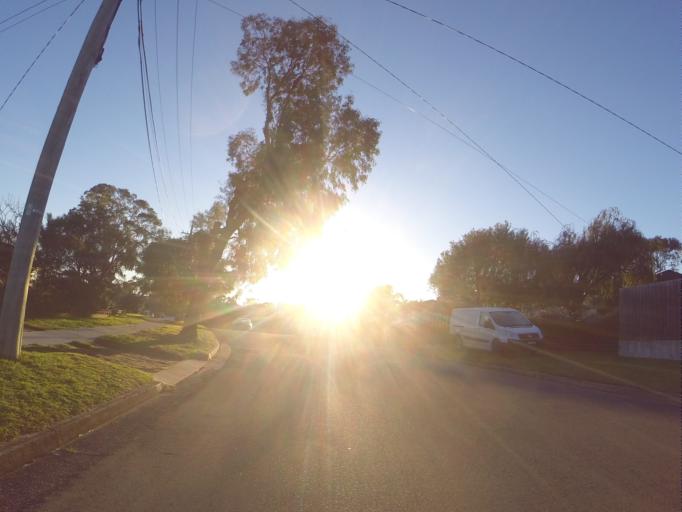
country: AU
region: New South Wales
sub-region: Sutherland Shire
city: Engadine
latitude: -34.0504
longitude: 151.0113
